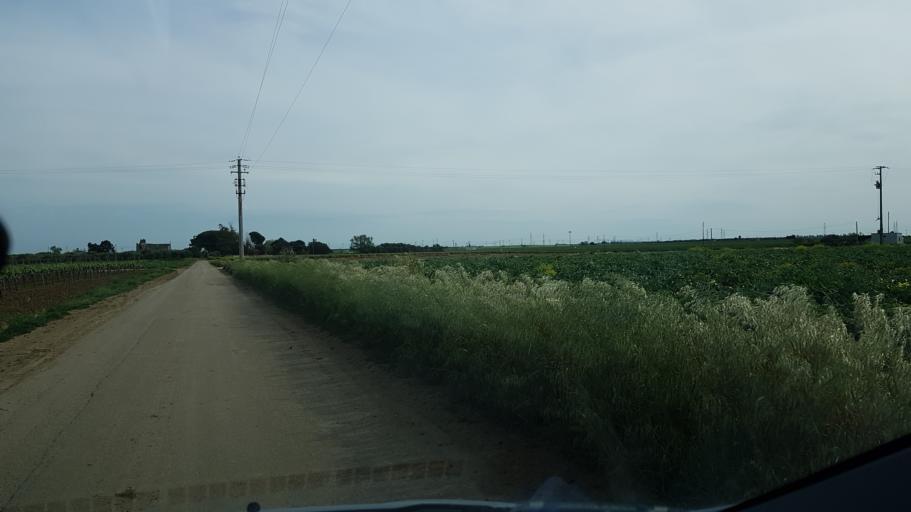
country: IT
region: Apulia
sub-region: Provincia di Brindisi
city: La Rosa
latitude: 40.5872
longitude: 17.9355
